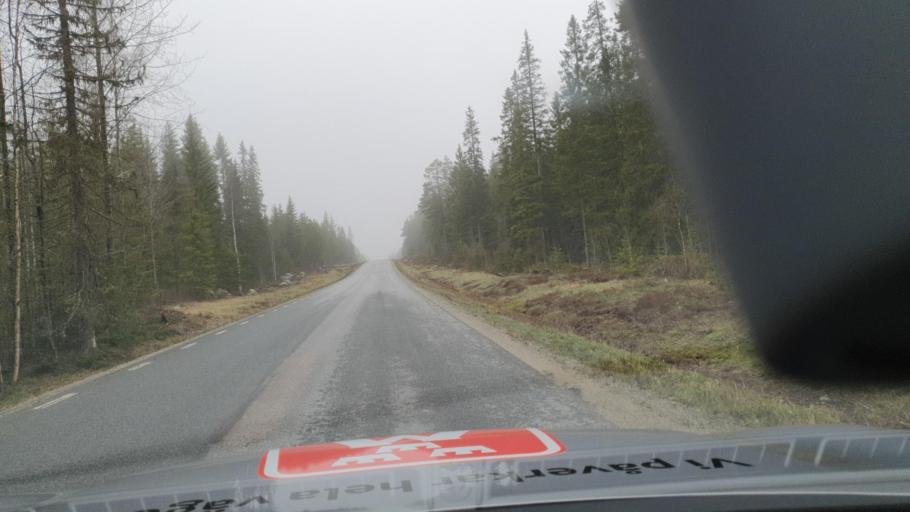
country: SE
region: Vaesternorrland
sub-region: OErnskoeldsviks Kommun
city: Husum
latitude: 63.4673
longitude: 19.2560
